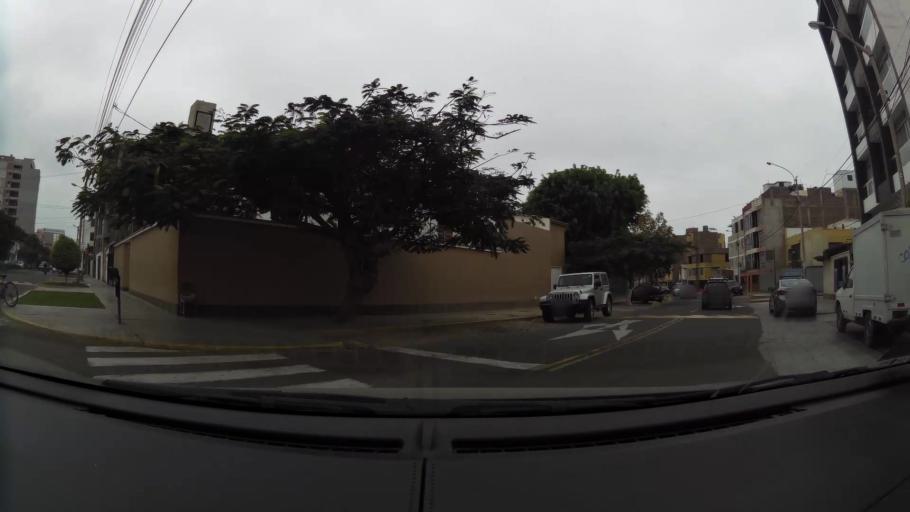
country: PE
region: La Libertad
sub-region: Provincia de Trujillo
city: Trujillo
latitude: -8.1188
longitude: -79.0382
